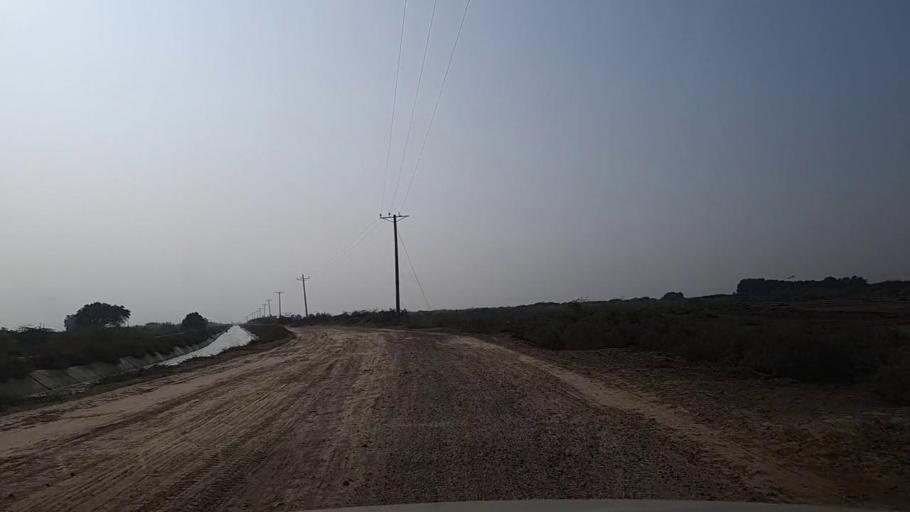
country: PK
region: Sindh
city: Keti Bandar
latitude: 24.1998
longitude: 67.6229
